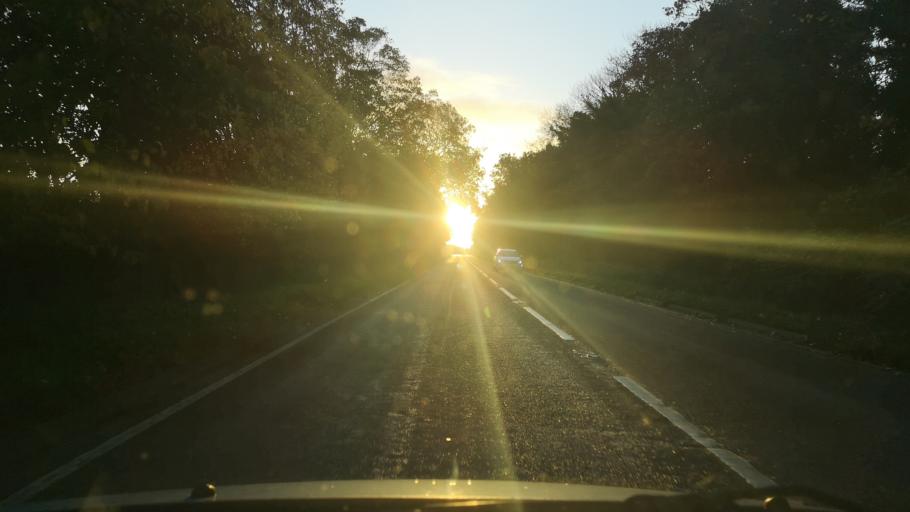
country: GB
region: England
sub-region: North Lincolnshire
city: Crowle
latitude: 53.5875
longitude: -0.8253
